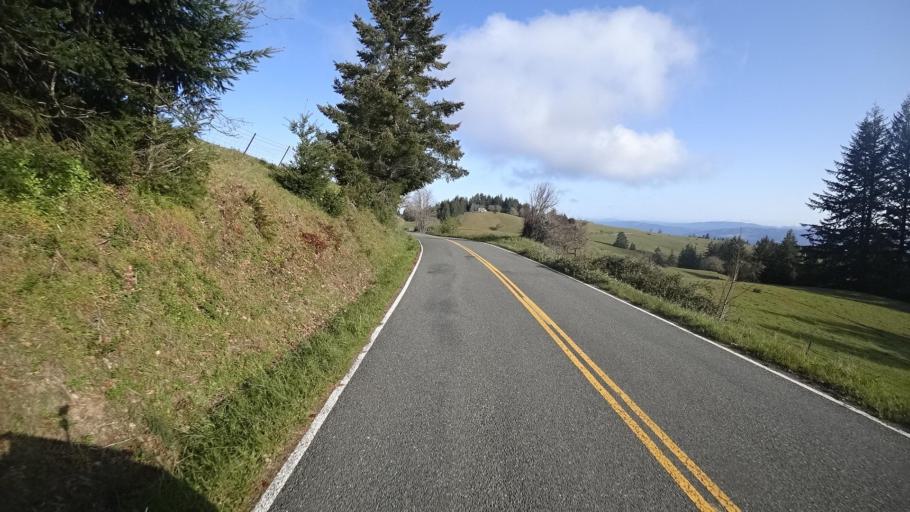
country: US
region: California
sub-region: Humboldt County
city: Blue Lake
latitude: 40.7284
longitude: -123.9459
